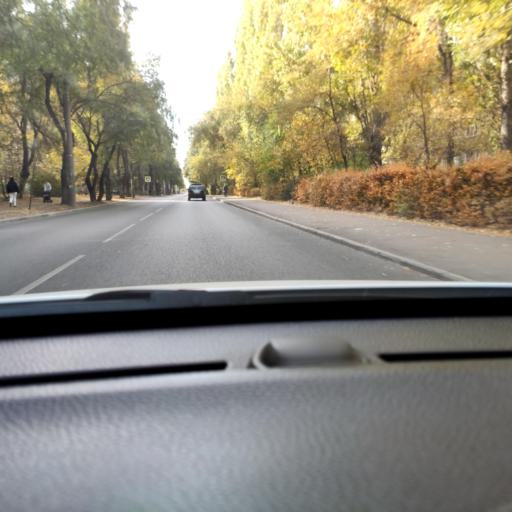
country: RU
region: Voronezj
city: Voronezh
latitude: 51.6932
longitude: 39.2626
